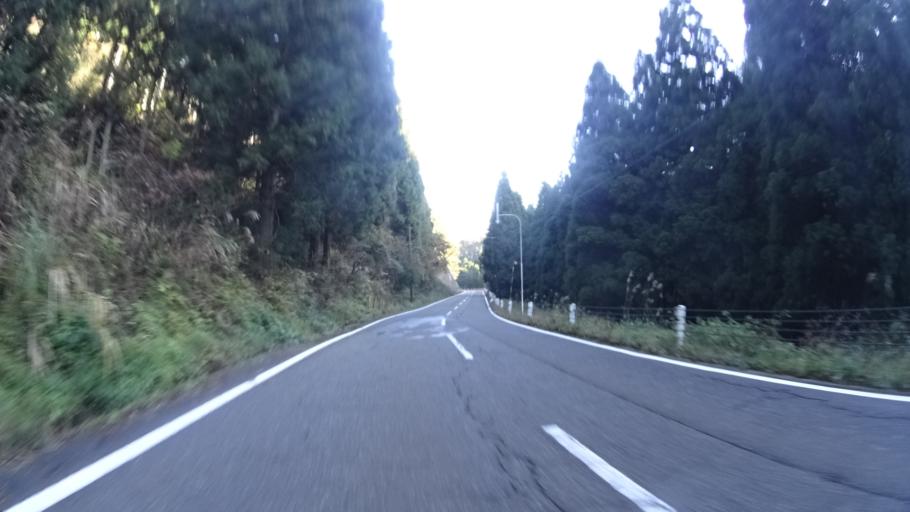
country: JP
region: Fukui
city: Maruoka
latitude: 36.1394
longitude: 136.3248
